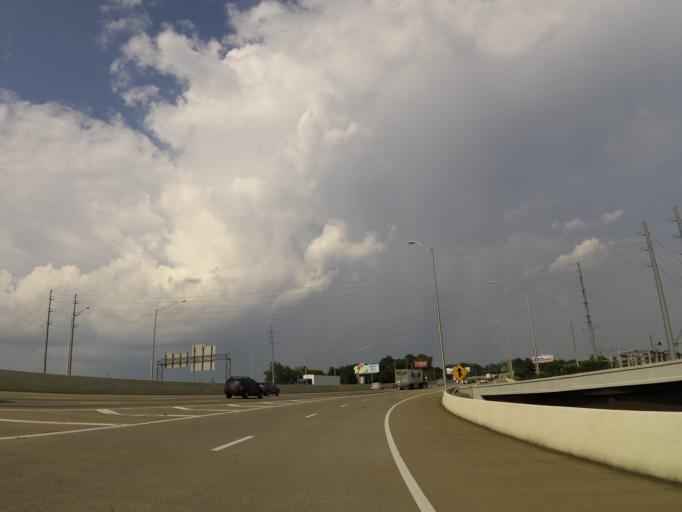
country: US
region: Tennessee
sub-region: Knox County
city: Knoxville
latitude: 35.9847
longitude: -83.9156
